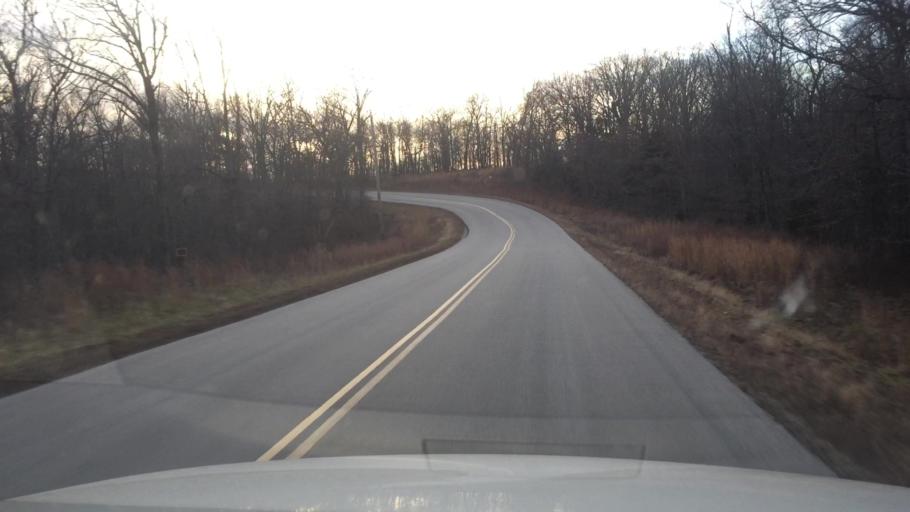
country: US
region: Missouri
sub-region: Morgan County
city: Versailles
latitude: 38.3306
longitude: -92.7741
